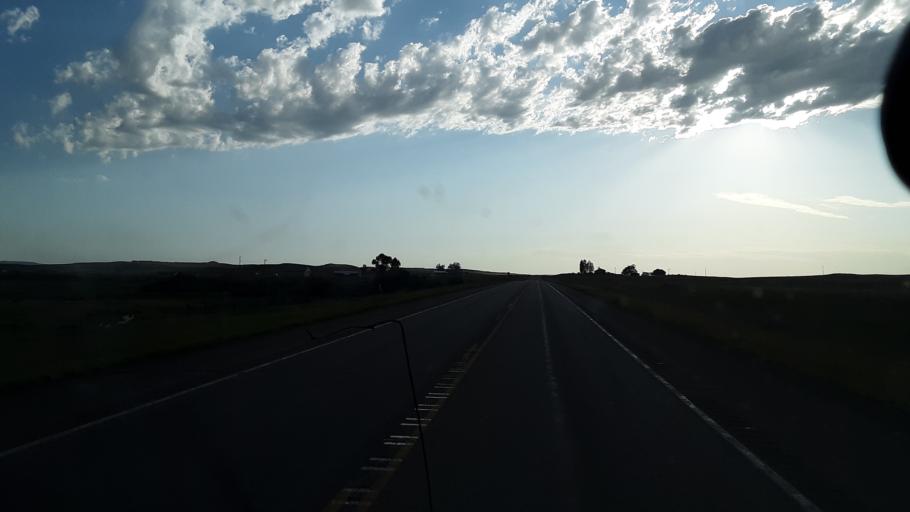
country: US
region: Montana
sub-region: Rosebud County
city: Lame Deer
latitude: 45.5286
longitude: -106.9693
